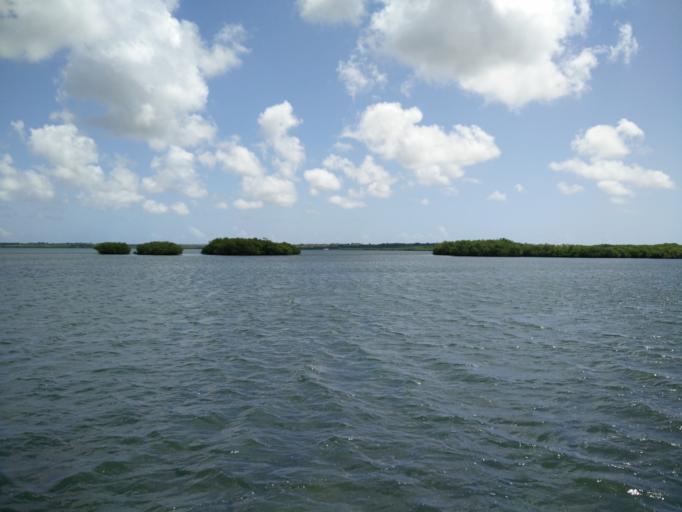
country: GP
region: Guadeloupe
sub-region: Guadeloupe
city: Petit-Canal
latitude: 16.3626
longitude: -61.5029
